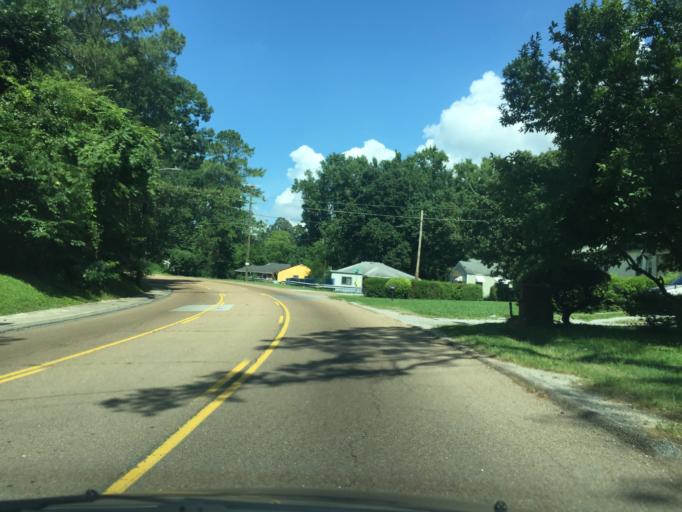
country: US
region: Tennessee
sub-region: Hamilton County
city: East Chattanooga
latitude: 35.0467
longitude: -85.2342
